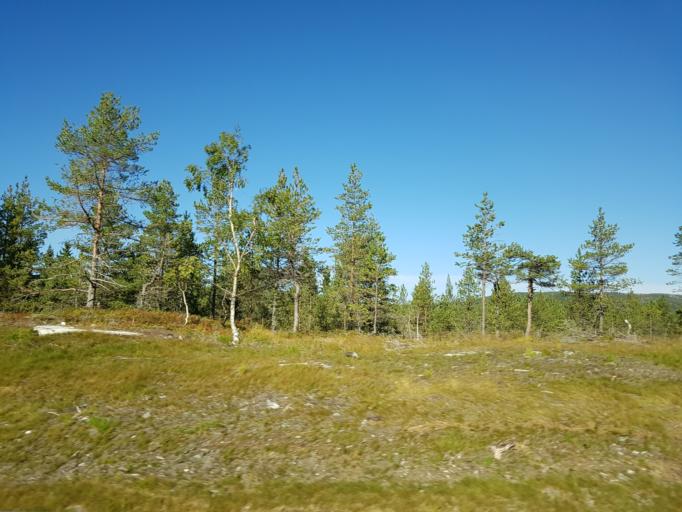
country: NO
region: Sor-Trondelag
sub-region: Afjord
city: A i Afjord
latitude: 63.7771
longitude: 10.2265
